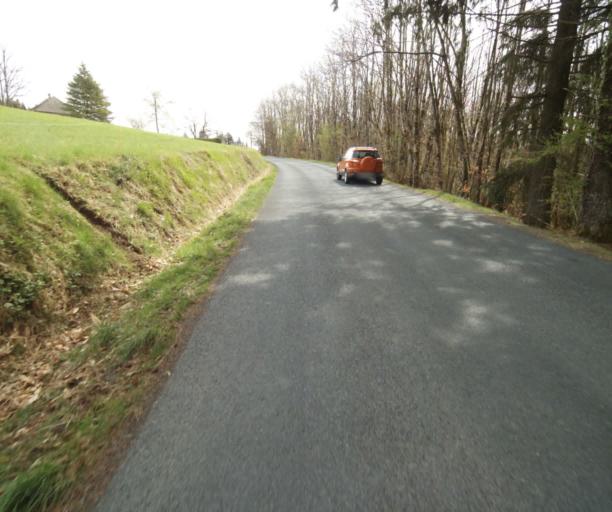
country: FR
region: Limousin
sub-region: Departement de la Correze
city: Sainte-Fortunade
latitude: 45.1986
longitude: 1.8360
